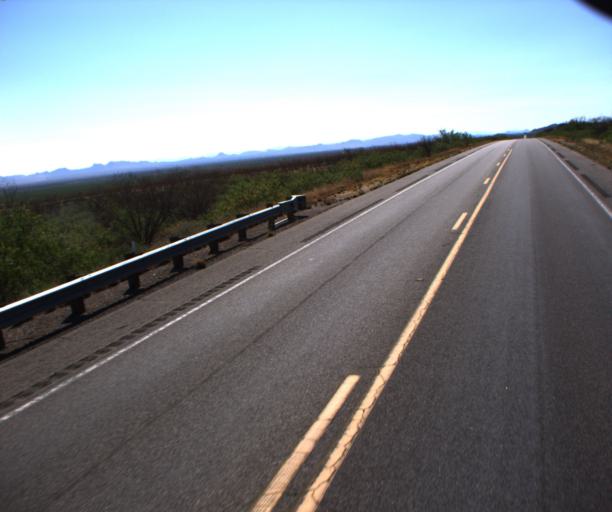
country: US
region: Arizona
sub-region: Cochise County
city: Bisbee
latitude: 31.4288
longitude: -109.8082
